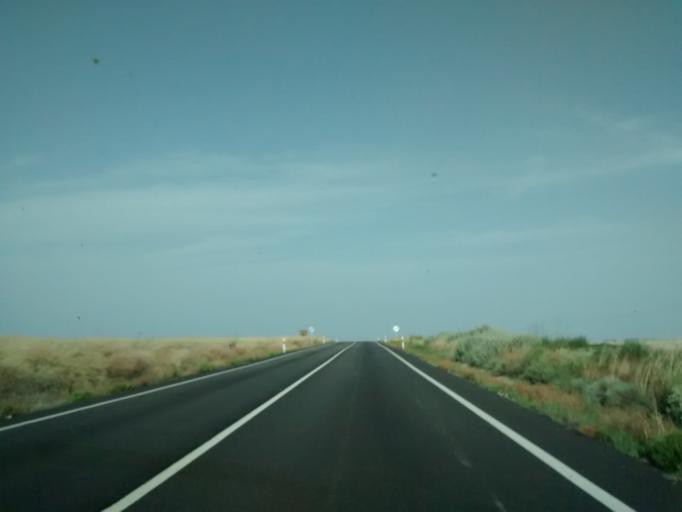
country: ES
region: Aragon
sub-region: Provincia de Zaragoza
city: Albeta
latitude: 41.8308
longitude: -1.4969
